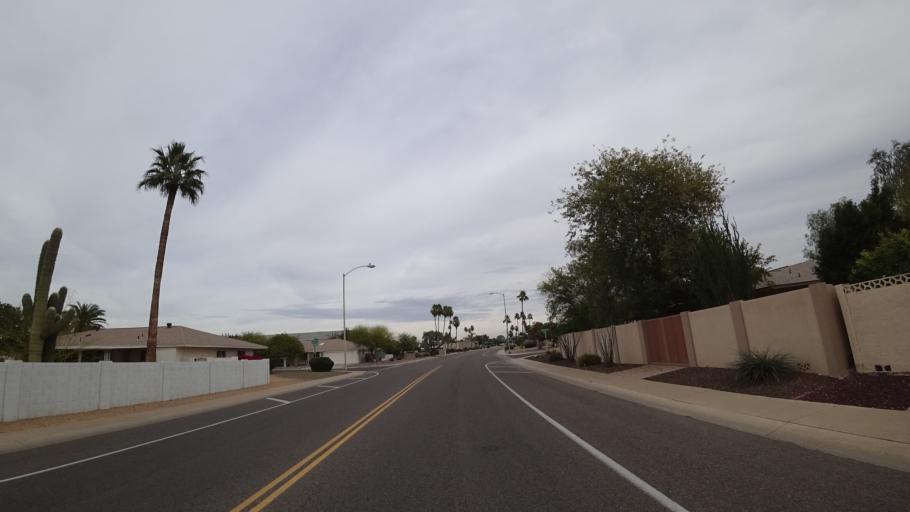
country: US
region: Arizona
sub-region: Maricopa County
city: Youngtown
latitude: 33.6173
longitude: -112.2942
